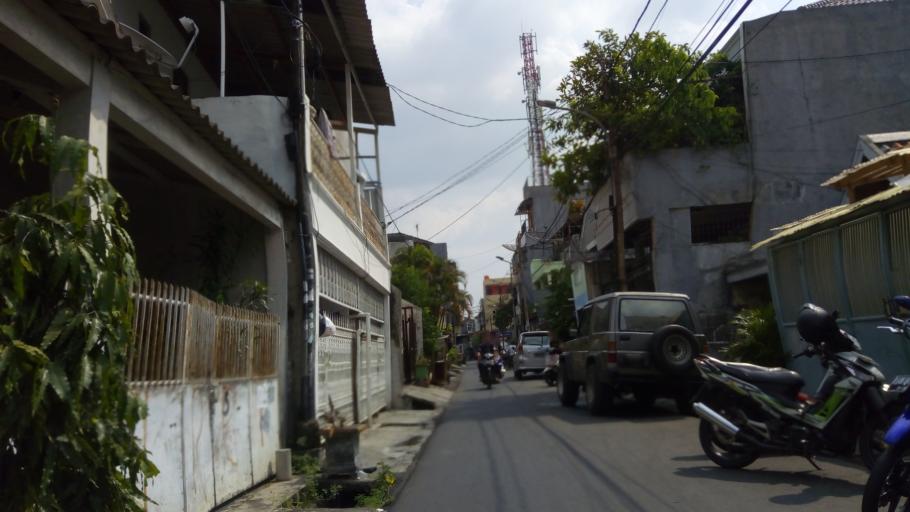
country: ID
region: Jakarta Raya
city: Jakarta
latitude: -6.1579
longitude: 106.8303
